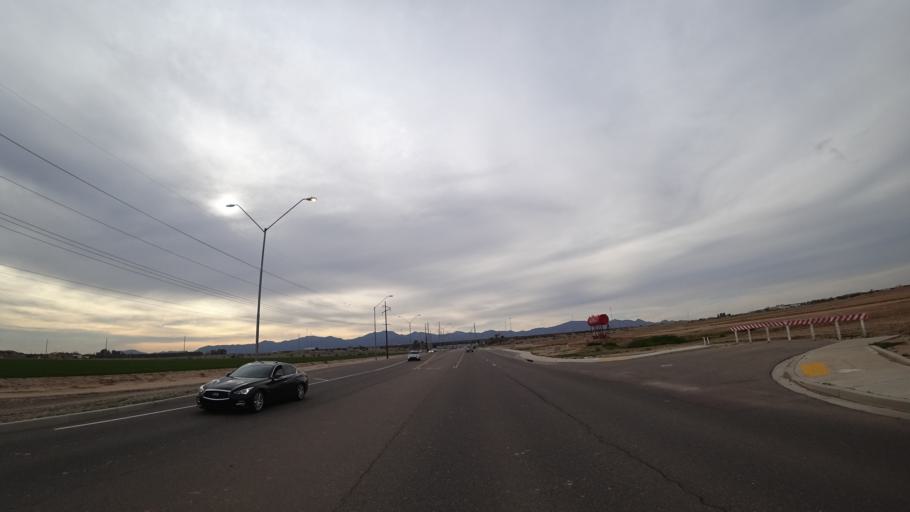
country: US
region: Arizona
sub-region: Maricopa County
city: Citrus Park
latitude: 33.5953
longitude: -112.4123
